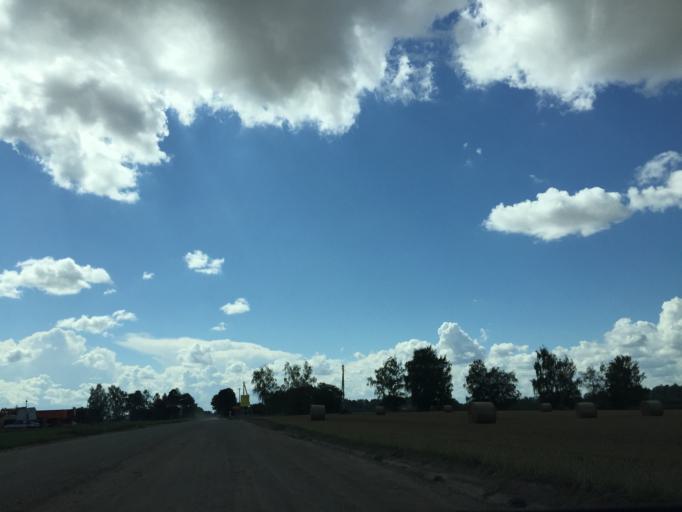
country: LV
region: Rundales
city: Pilsrundale
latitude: 56.3014
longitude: 24.0000
